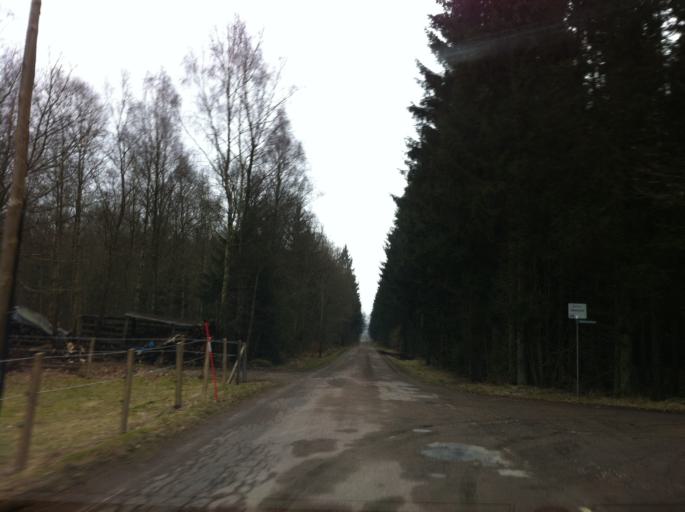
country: SE
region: Skane
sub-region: Svalovs Kommun
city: Kagerod
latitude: 56.0192
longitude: 13.1645
